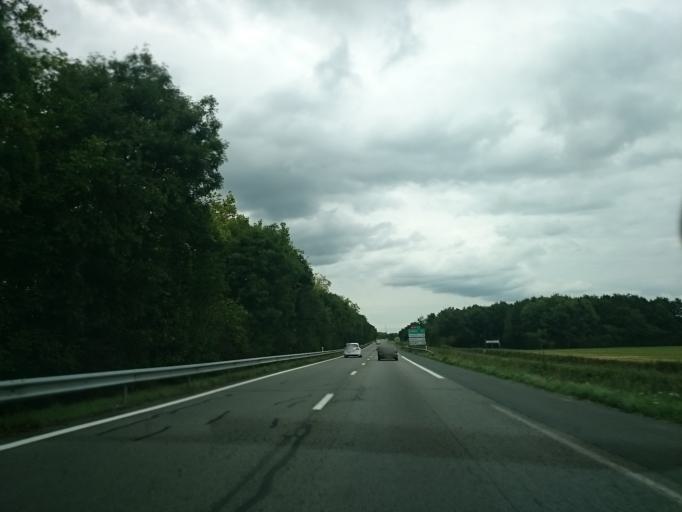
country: FR
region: Pays de la Loire
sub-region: Departement de la Loire-Atlantique
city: Heric
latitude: 47.3831
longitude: -1.6430
